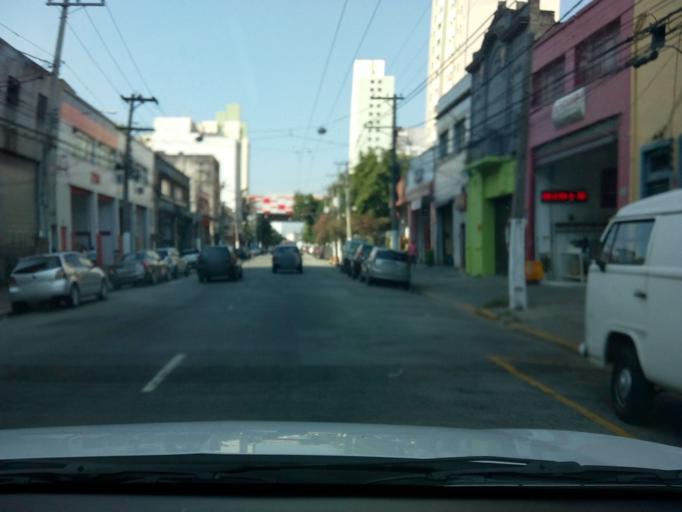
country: BR
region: Sao Paulo
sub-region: Sao Paulo
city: Sao Paulo
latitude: -23.5470
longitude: -46.6198
